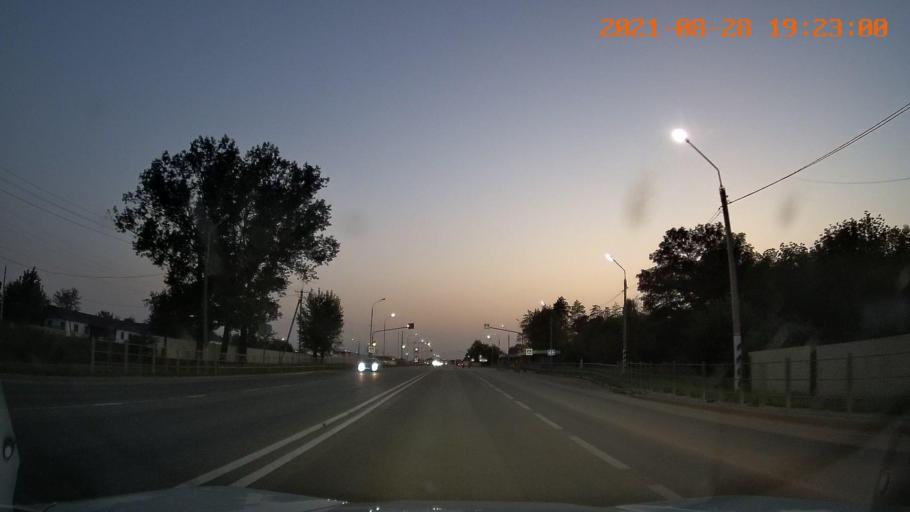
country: RU
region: Adygeya
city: Ponezhukay
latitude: 44.8757
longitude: 39.4550
